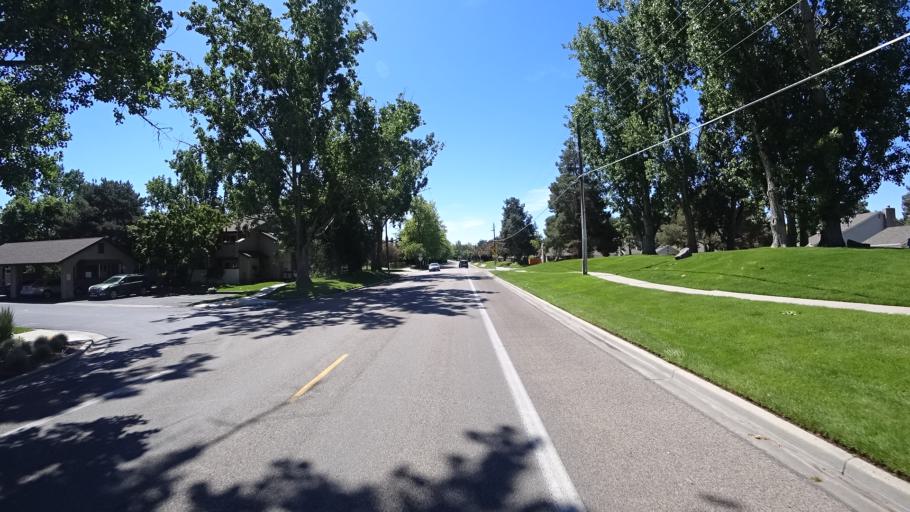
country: US
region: Idaho
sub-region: Ada County
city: Boise
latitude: 43.5741
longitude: -116.1836
